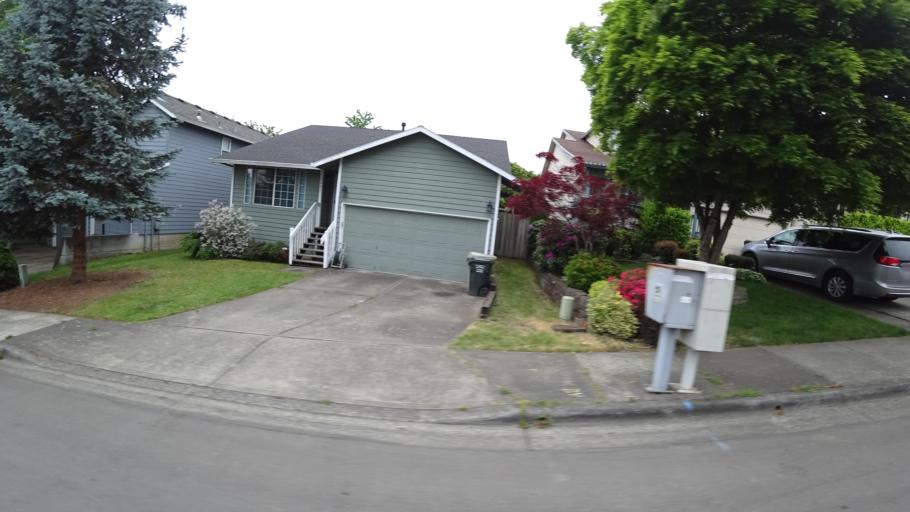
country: US
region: Oregon
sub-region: Washington County
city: Bethany
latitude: 45.5590
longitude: -122.8630
